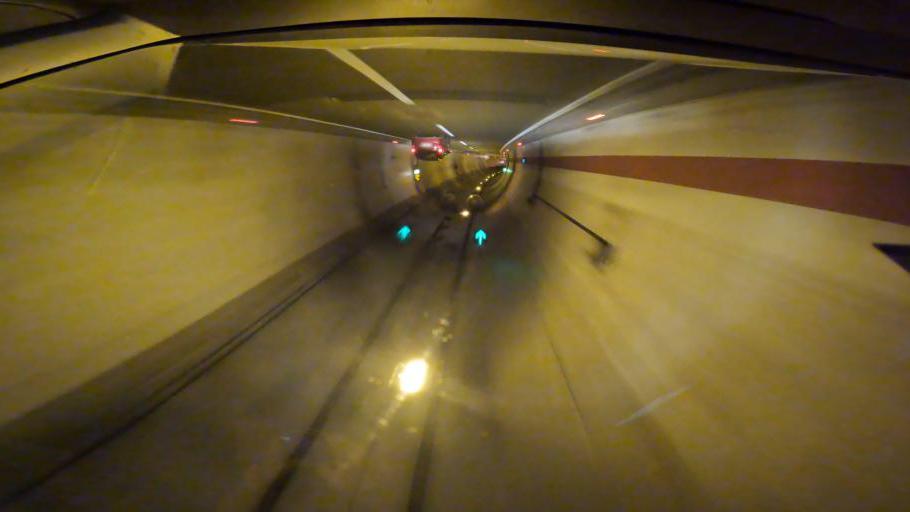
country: HR
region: Primorsko-Goranska
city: Hreljin
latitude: 45.3261
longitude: 14.6528
